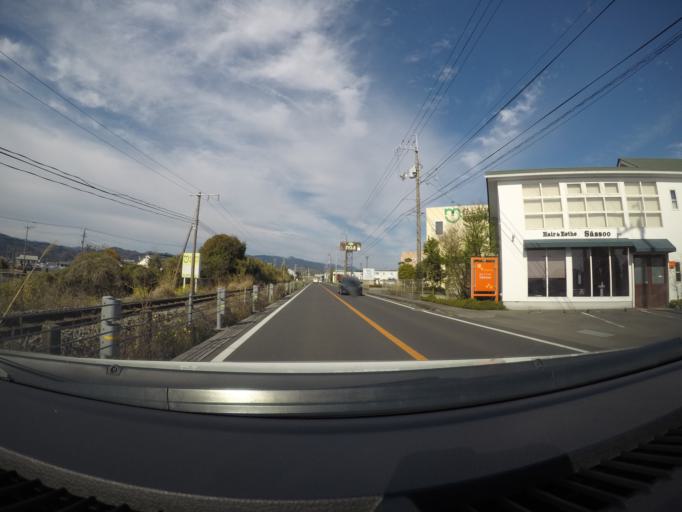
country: JP
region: Kochi
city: Kochi-shi
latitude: 33.5996
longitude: 133.6715
